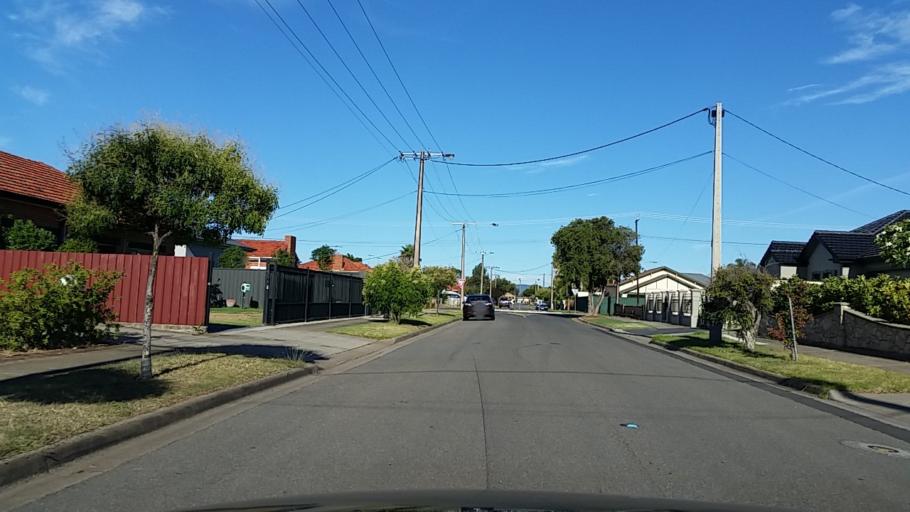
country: AU
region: South Australia
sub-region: Charles Sturt
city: Seaton
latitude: -34.8898
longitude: 138.5188
